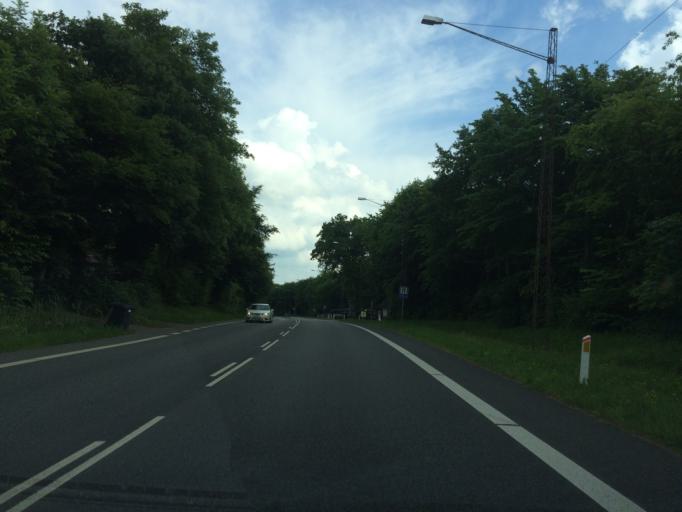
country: DK
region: South Denmark
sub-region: Middelfart Kommune
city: Middelfart
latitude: 55.5030
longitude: 9.7071
